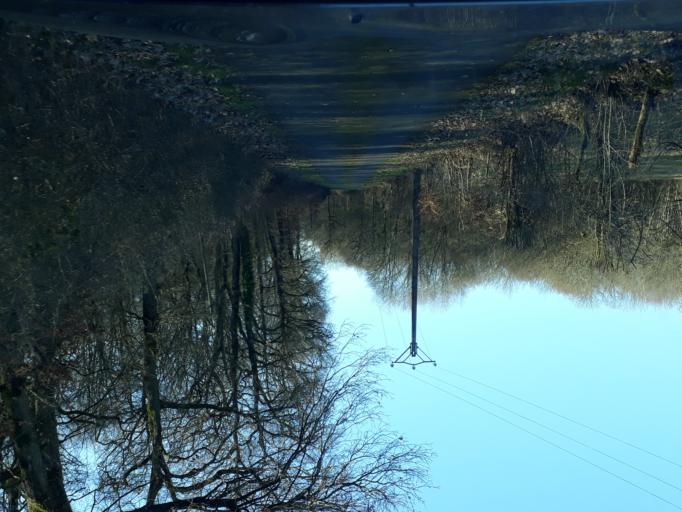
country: FR
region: Centre
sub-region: Departement du Loir-et-Cher
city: Oucques
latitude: 47.8779
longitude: 1.3719
